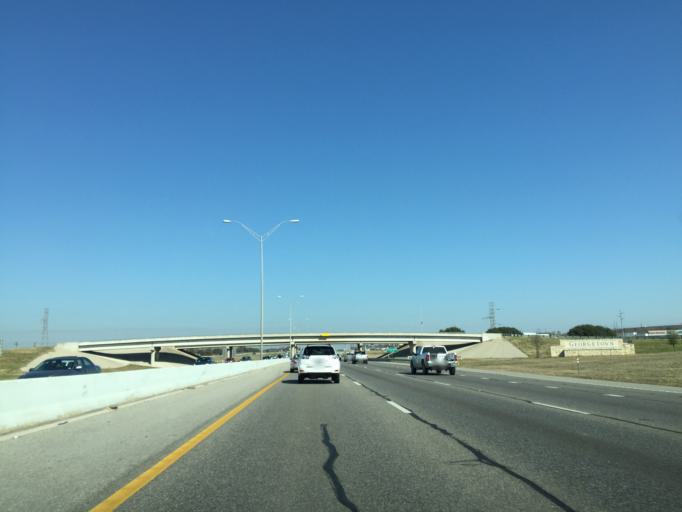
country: US
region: Texas
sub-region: Williamson County
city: Georgetown
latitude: 30.5755
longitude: -97.6926
